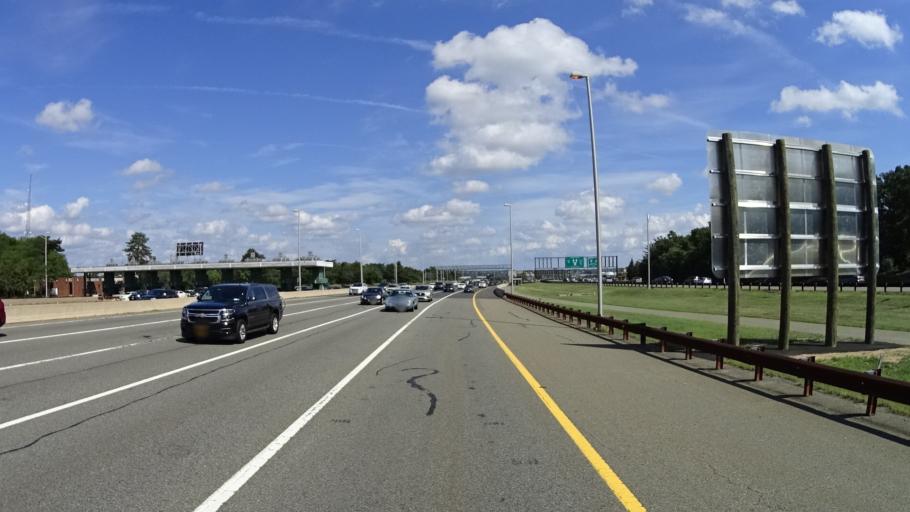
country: US
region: New Jersey
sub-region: Middlesex County
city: South Amboy
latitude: 40.4847
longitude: -74.3028
